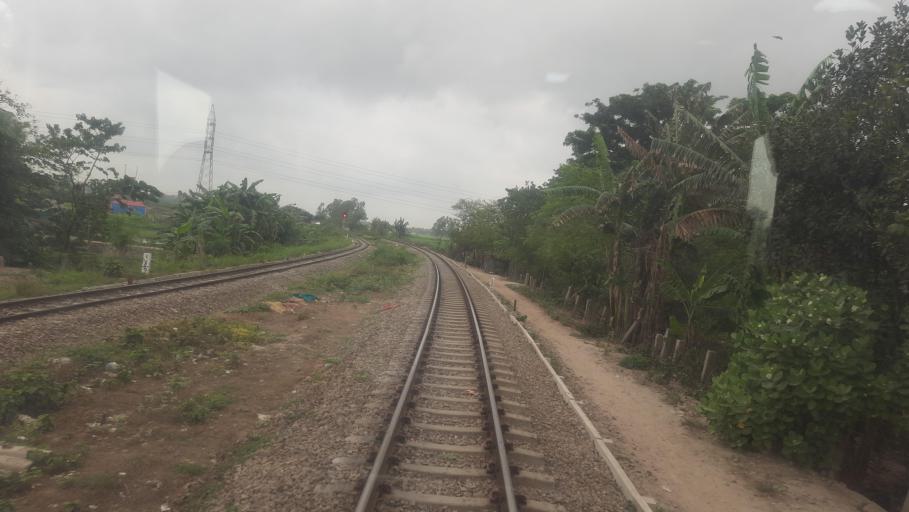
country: BD
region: Dhaka
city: Bhairab Bazar
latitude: 24.0502
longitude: 90.9721
